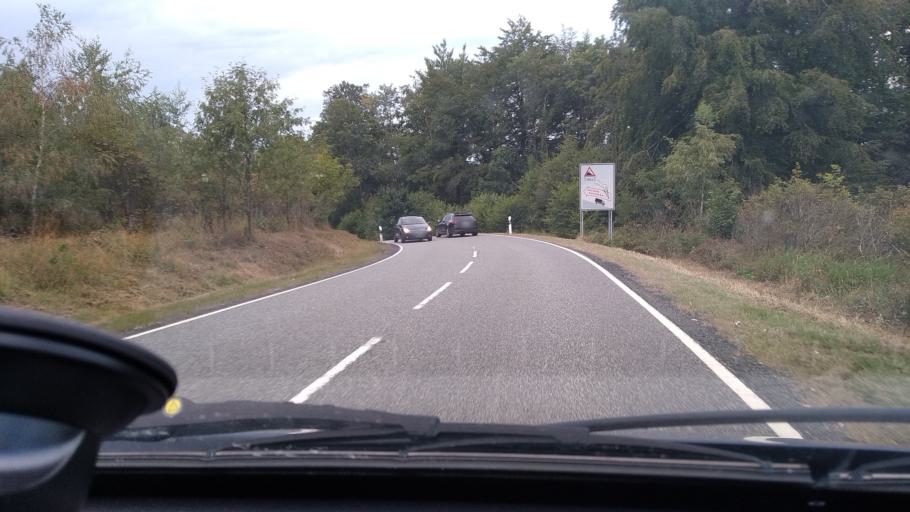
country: DE
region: Hesse
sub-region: Regierungsbezirk Giessen
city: Siegbach
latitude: 50.7895
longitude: 8.3790
